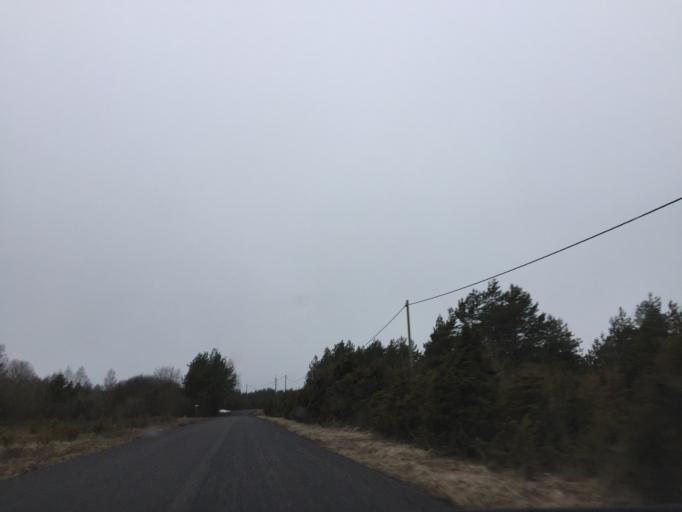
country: EE
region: Laeaene
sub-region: Lihula vald
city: Lihula
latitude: 58.6572
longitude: 23.5921
